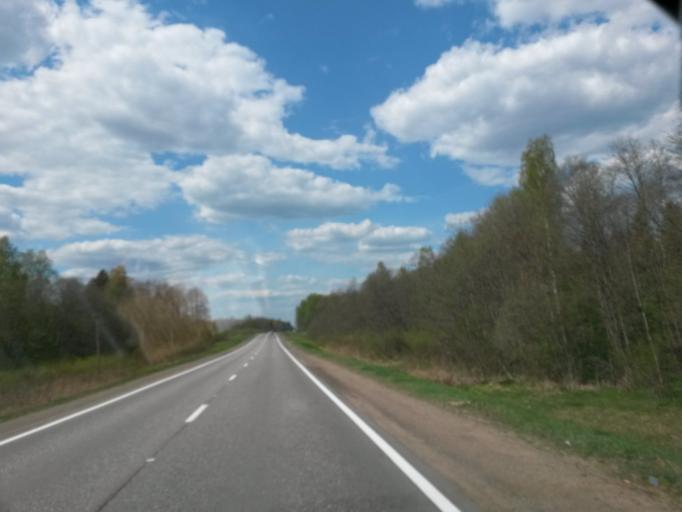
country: RU
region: Jaroslavl
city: Bol'shoye Selo
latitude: 57.7156
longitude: 39.1118
